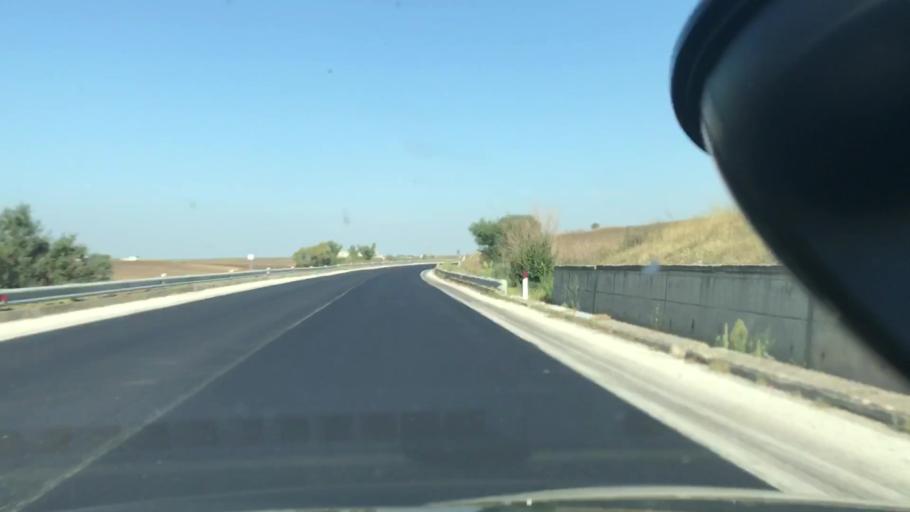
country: IT
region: Apulia
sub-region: Provincia di Barletta - Andria - Trani
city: Spinazzola
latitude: 40.9071
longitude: 16.1100
